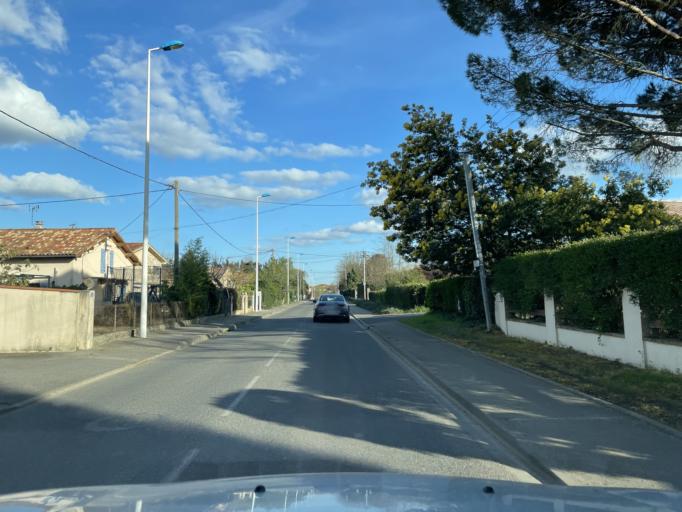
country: FR
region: Midi-Pyrenees
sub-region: Departement de la Haute-Garonne
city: Leguevin
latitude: 43.6025
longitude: 1.2271
